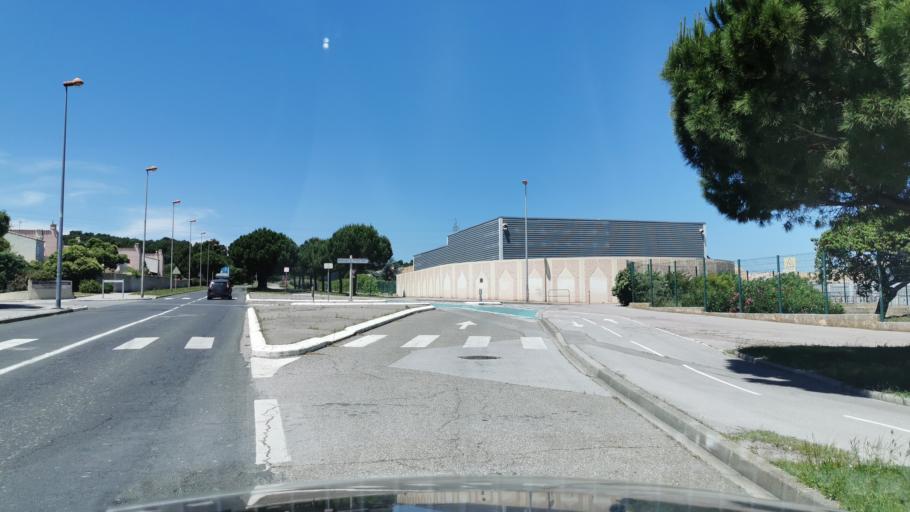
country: FR
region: Languedoc-Roussillon
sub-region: Departement de l'Aude
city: Narbonne
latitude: 43.1851
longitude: 2.9749
